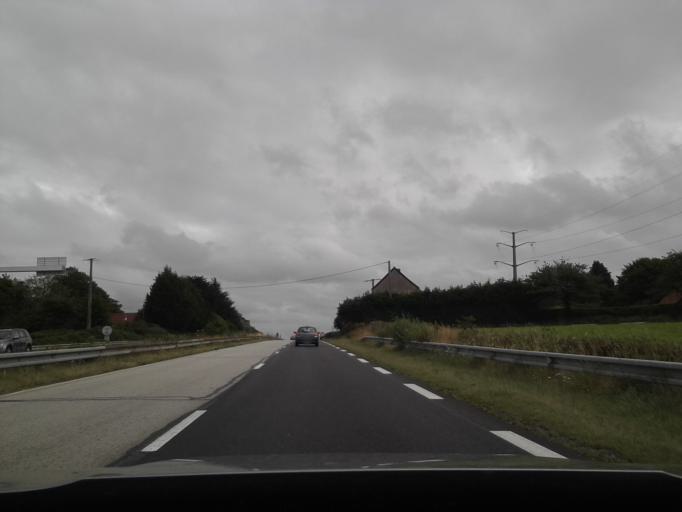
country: FR
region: Lower Normandy
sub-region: Departement de la Manche
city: La Glacerie
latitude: 49.5843
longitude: -1.5929
